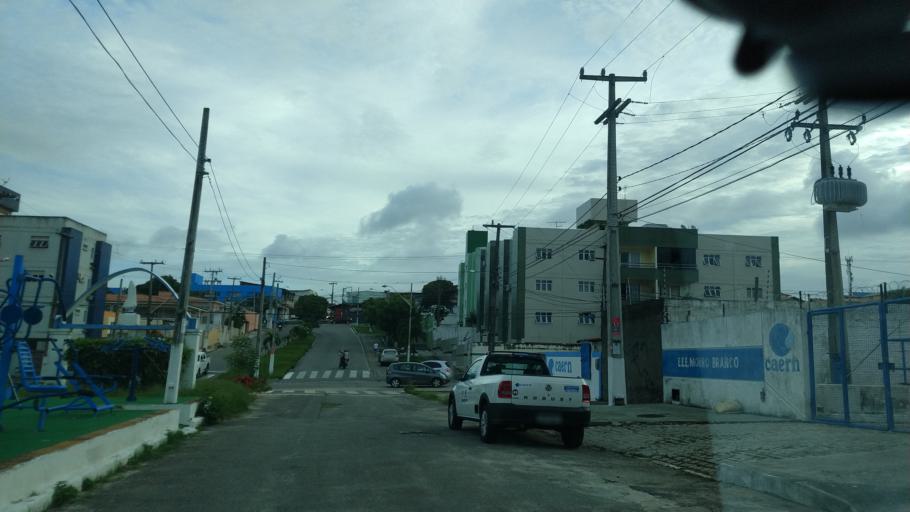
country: BR
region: Rio Grande do Norte
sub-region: Natal
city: Natal
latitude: -5.8229
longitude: -35.1994
